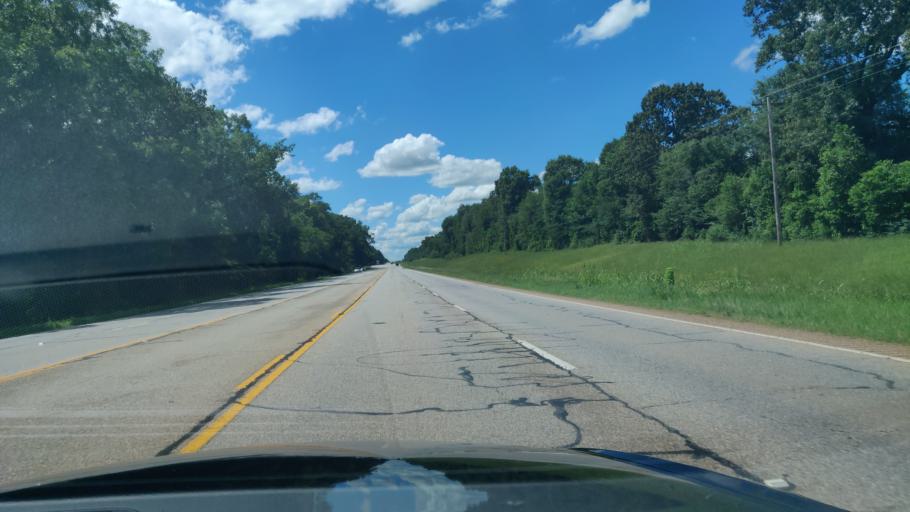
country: US
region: Georgia
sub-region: Webster County
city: Preston
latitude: 31.9727
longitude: -84.6106
